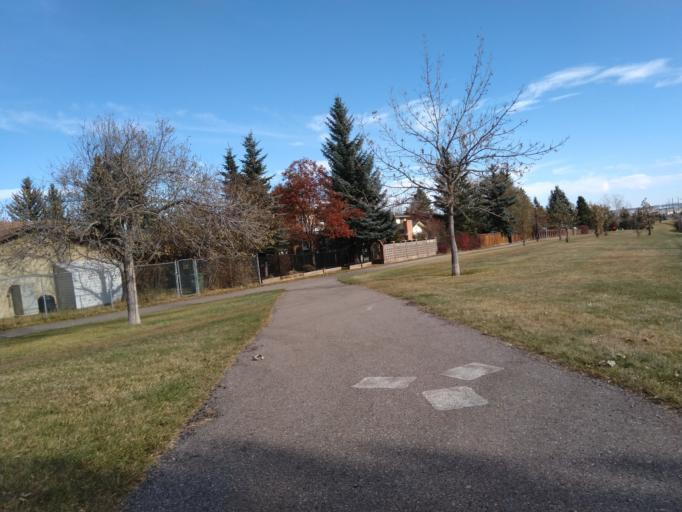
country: CA
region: Alberta
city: Calgary
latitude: 51.1250
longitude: -114.0833
